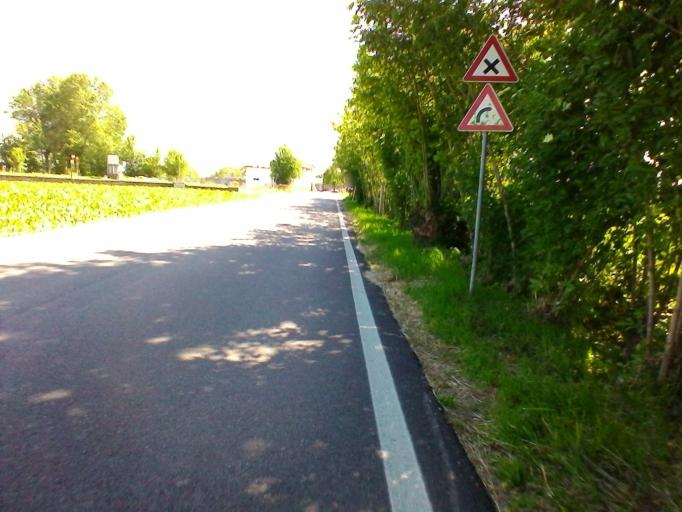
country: IT
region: Veneto
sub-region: Provincia di Verona
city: Povegliano Veronese
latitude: 45.3395
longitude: 10.8802
